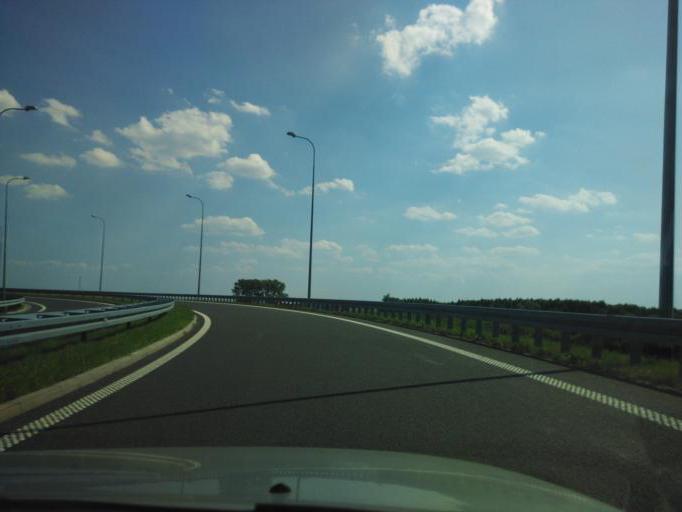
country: PL
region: West Pomeranian Voivodeship
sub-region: Powiat gryfinski
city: Banie
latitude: 53.1236
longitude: 14.7354
